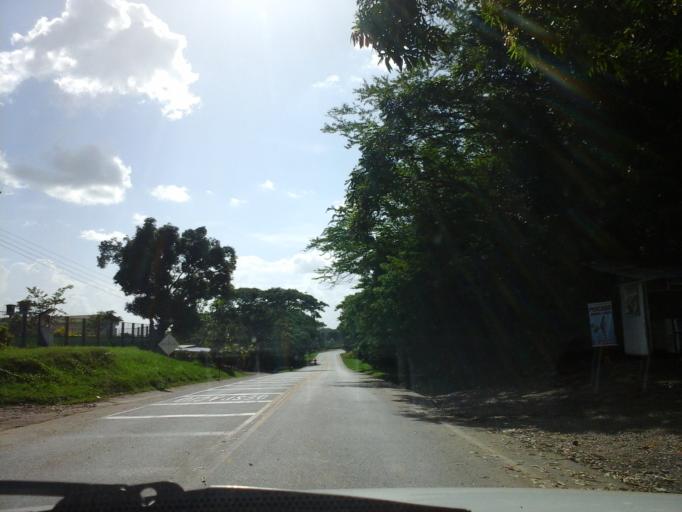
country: CO
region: Meta
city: Puerto Lopez
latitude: 4.0569
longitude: -73.0500
